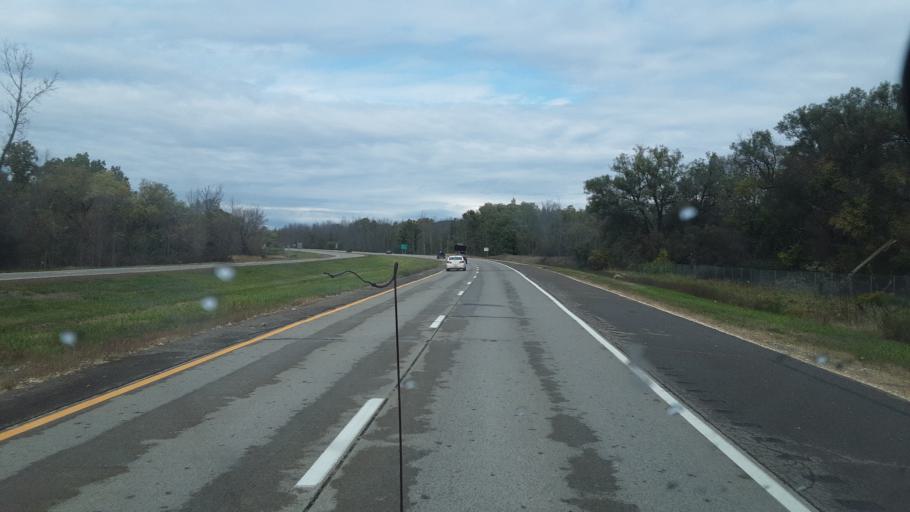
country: US
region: New York
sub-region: Steuben County
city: Hornell
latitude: 42.3556
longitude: -77.6686
